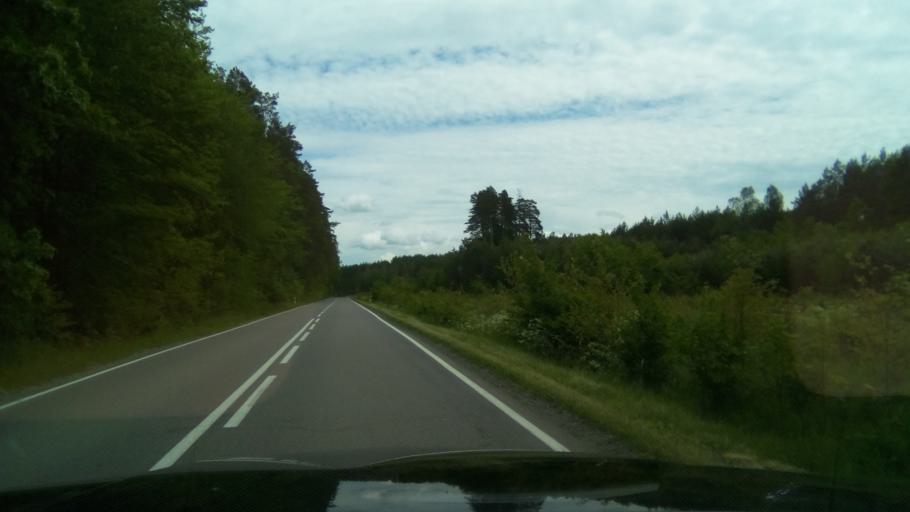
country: PL
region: Pomeranian Voivodeship
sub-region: Powiat bytowski
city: Czarna Dabrowka
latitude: 54.3645
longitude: 17.5916
